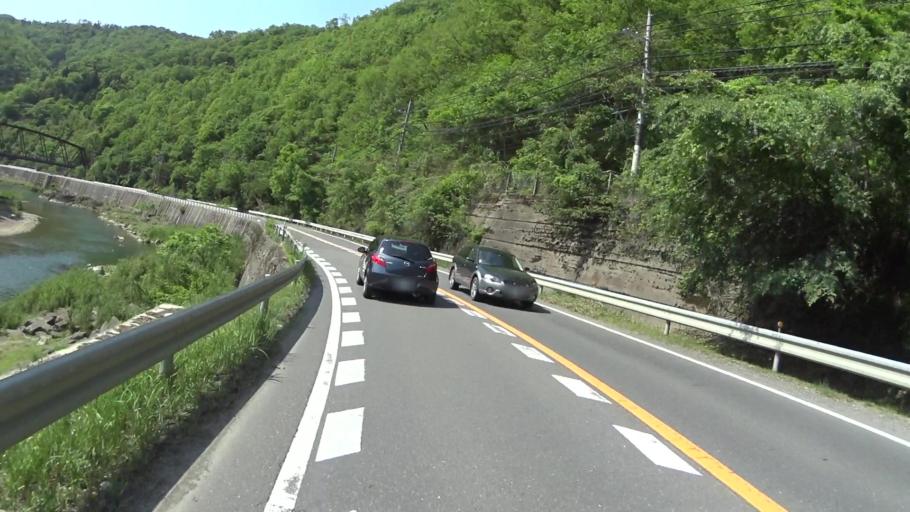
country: JP
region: Kyoto
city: Kameoka
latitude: 35.1450
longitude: 135.5016
